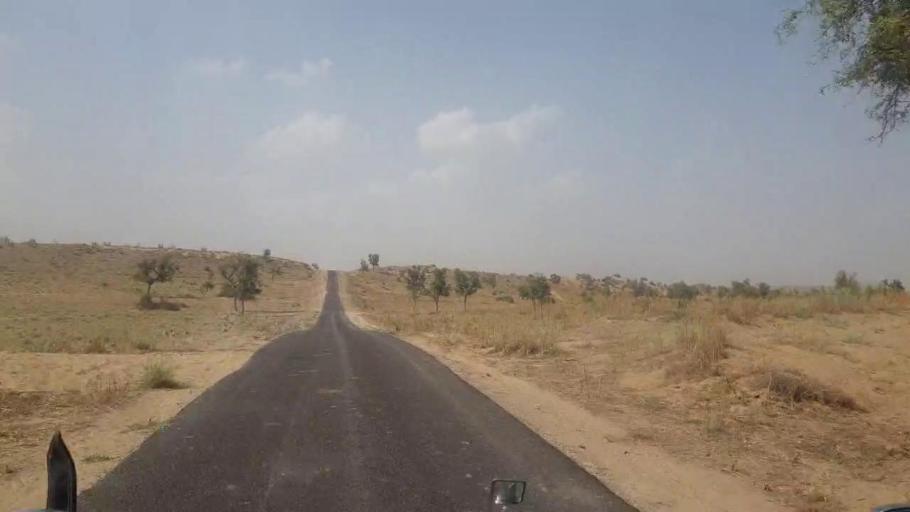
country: PK
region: Sindh
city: Islamkot
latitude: 25.1908
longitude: 70.2855
